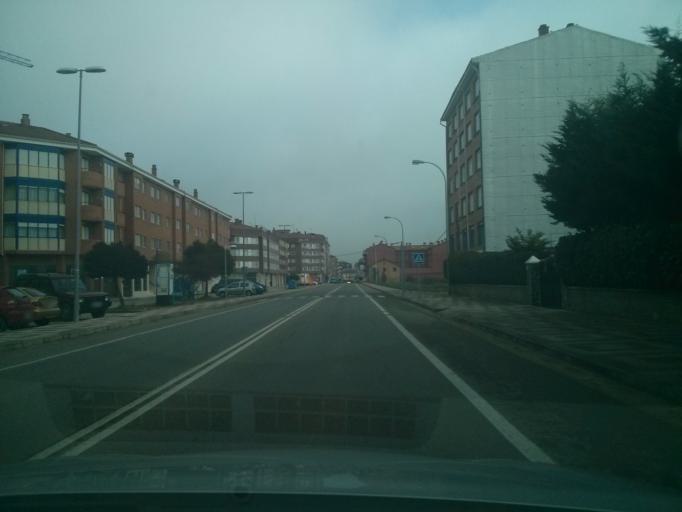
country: ES
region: Castille and Leon
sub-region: Provincia de Burgos
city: Medina de Pomar
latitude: 42.9331
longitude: -3.4931
